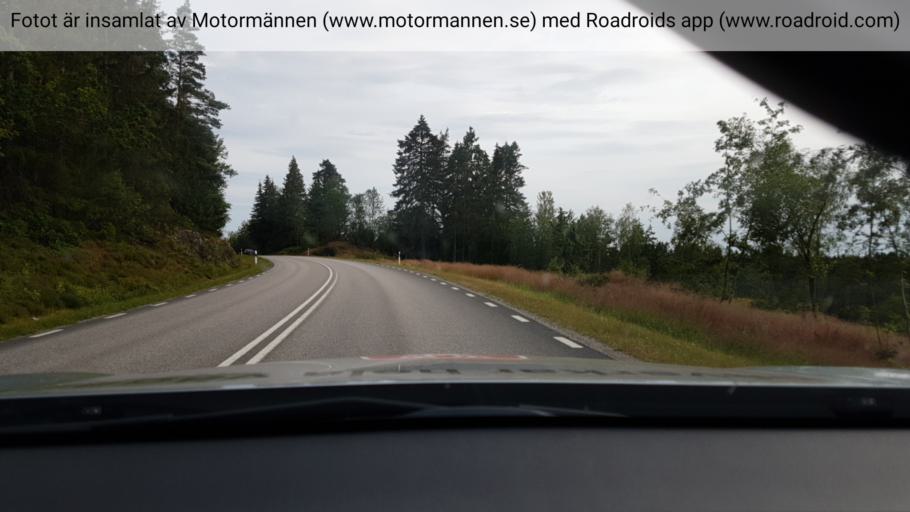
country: SE
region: Vaestra Goetaland
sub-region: Uddevalla Kommun
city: Uddevalla
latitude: 58.4393
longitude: 12.0169
